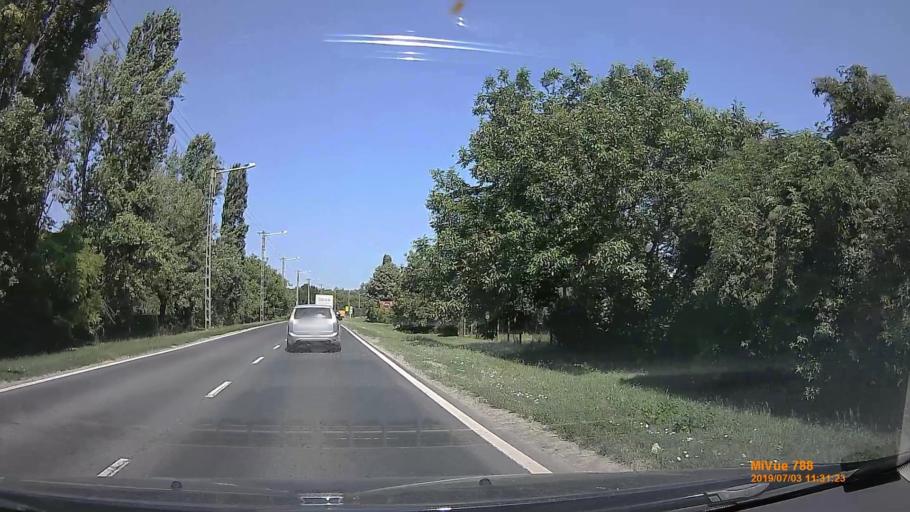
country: HU
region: Gyor-Moson-Sopron
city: Gyor
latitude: 47.7010
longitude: 17.6350
